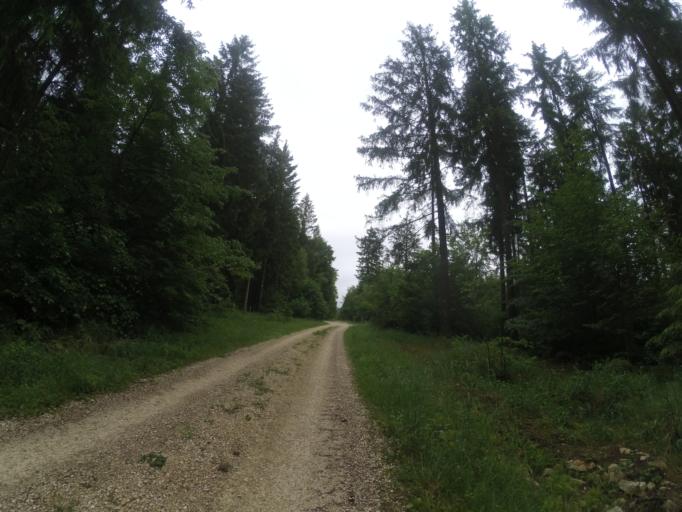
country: DE
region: Baden-Wuerttemberg
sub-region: Tuebingen Region
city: Borslingen
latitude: 48.5200
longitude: 10.0590
